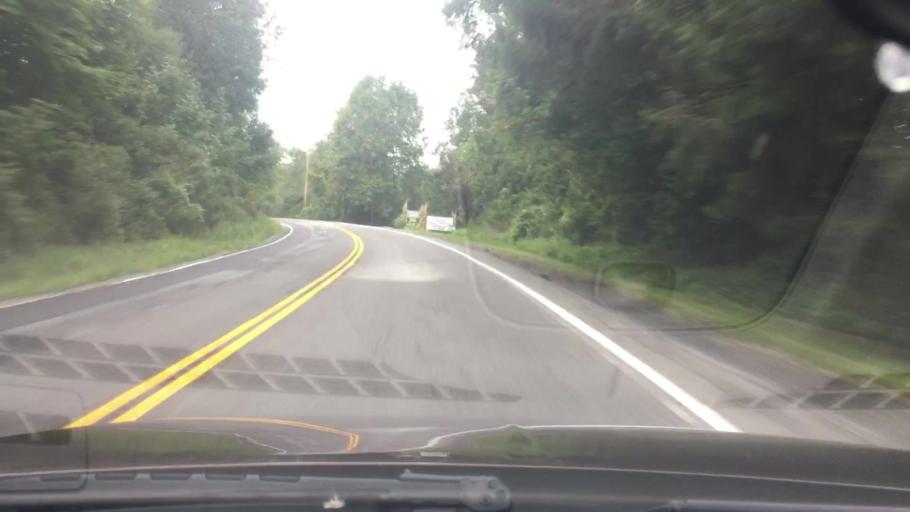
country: US
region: New York
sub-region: Dutchess County
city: Millbrook
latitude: 41.7942
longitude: -73.7129
